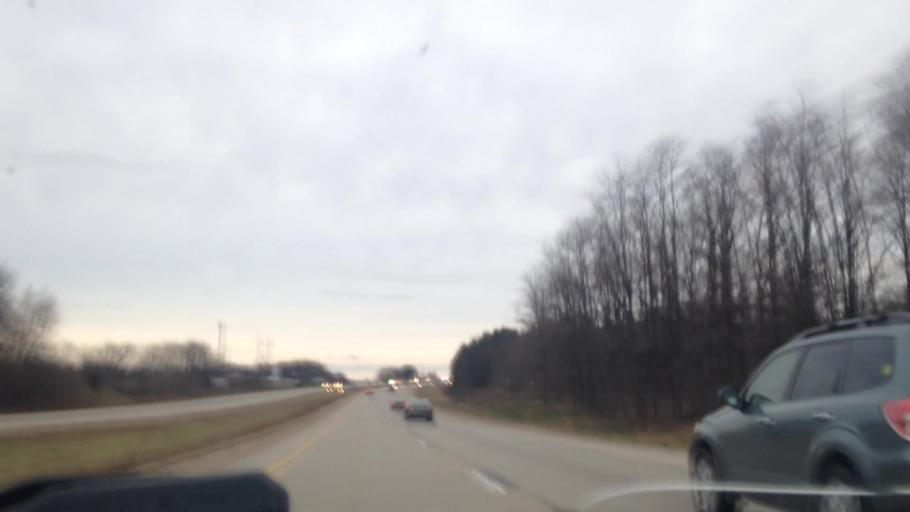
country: US
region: Wisconsin
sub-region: Washington County
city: Slinger
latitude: 43.3540
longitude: -88.2875
